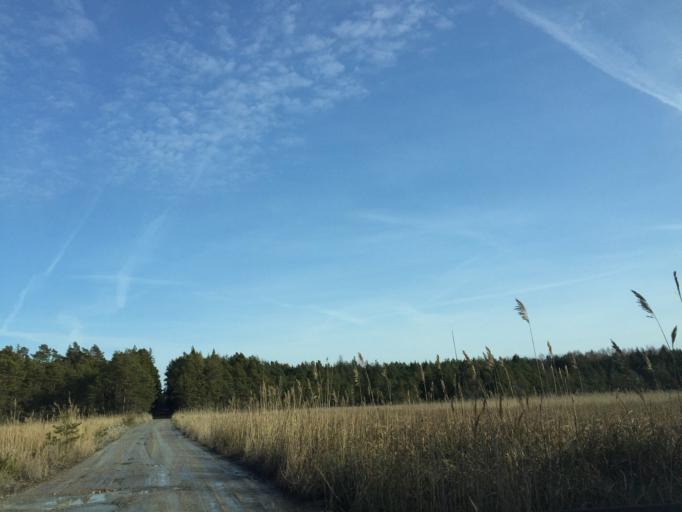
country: EE
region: Saare
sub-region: Kuressaare linn
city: Kuressaare
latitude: 58.3767
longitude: 22.0048
